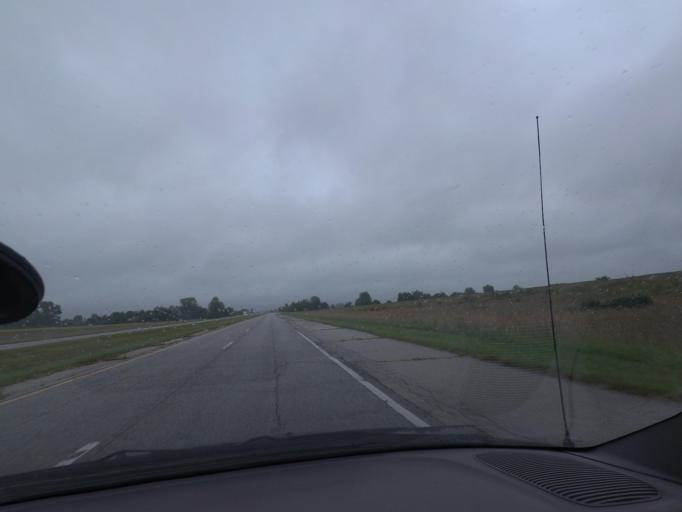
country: US
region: Illinois
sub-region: Pike County
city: Pittsfield
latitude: 39.6713
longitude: -90.8375
